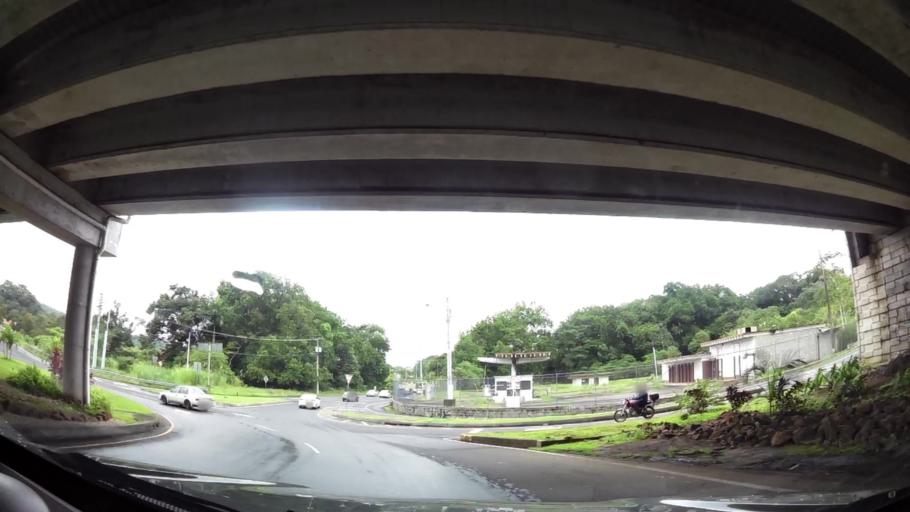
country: PA
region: Panama
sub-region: Distrito de Panama
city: Ancon
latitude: 8.9916
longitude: -79.5530
